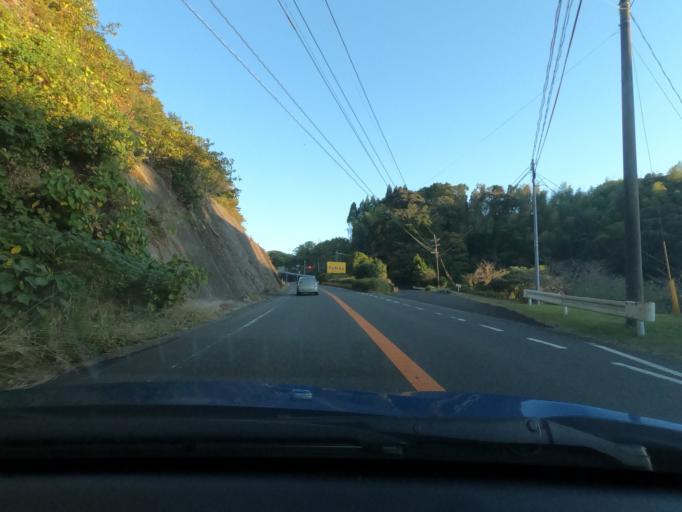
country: JP
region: Kagoshima
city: Satsumasendai
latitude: 31.7970
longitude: 130.4202
